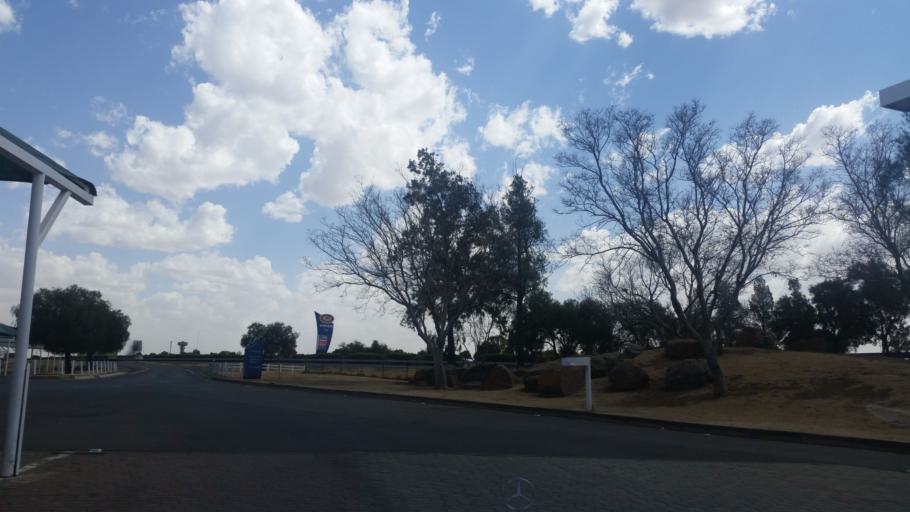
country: ZA
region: Orange Free State
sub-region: Mangaung Metropolitan Municipality
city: Bloemfontein
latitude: -29.0751
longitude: 26.1826
